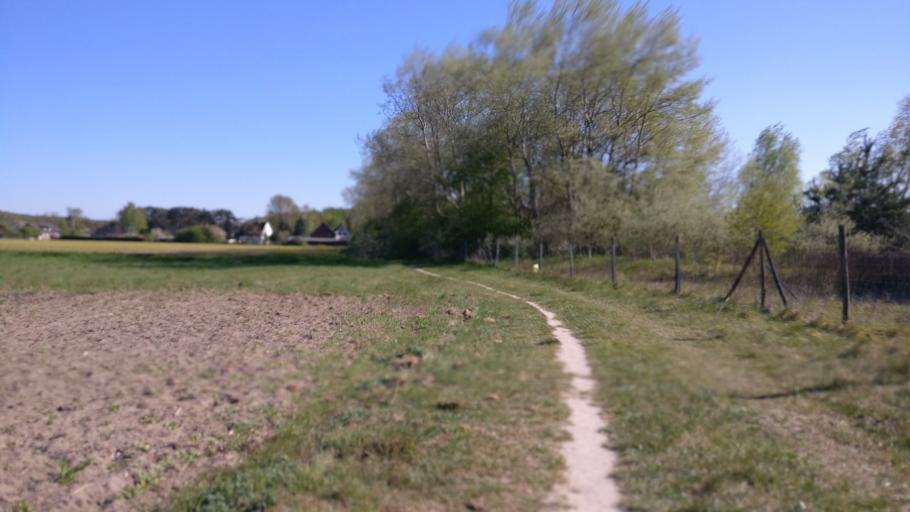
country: DE
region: North Rhine-Westphalia
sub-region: Regierungsbezirk Detmold
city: Lage
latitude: 52.0183
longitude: 8.7593
